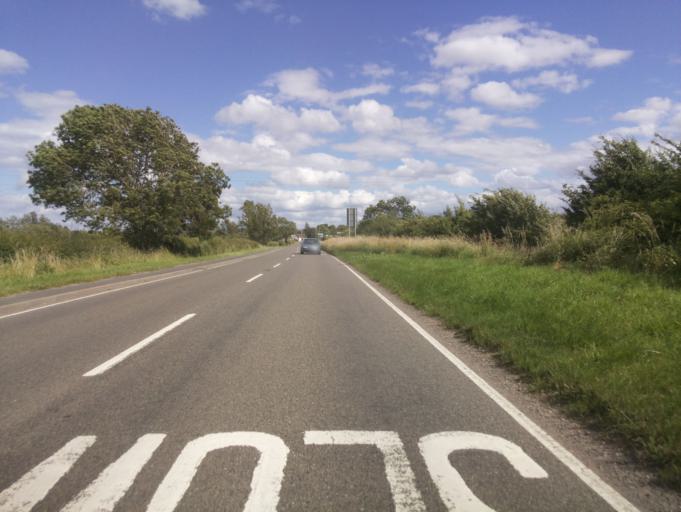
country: GB
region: England
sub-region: Leicestershire
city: Hathern
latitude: 52.8012
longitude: -1.2673
